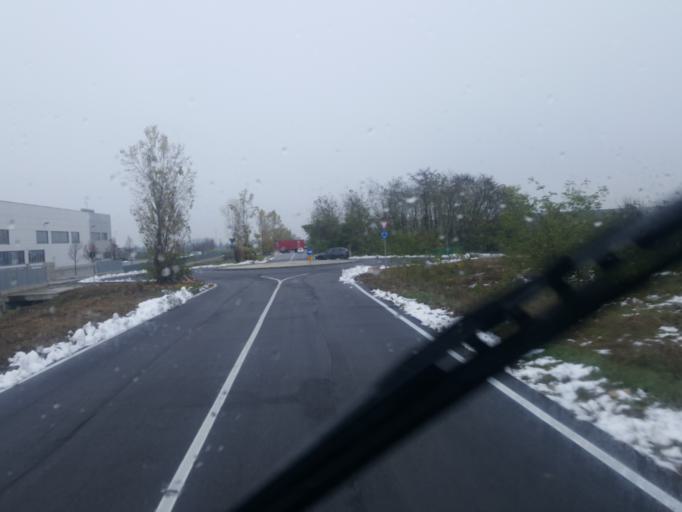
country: IT
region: Piedmont
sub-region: Provincia di Cuneo
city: Breo
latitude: 44.4038
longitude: 7.8257
